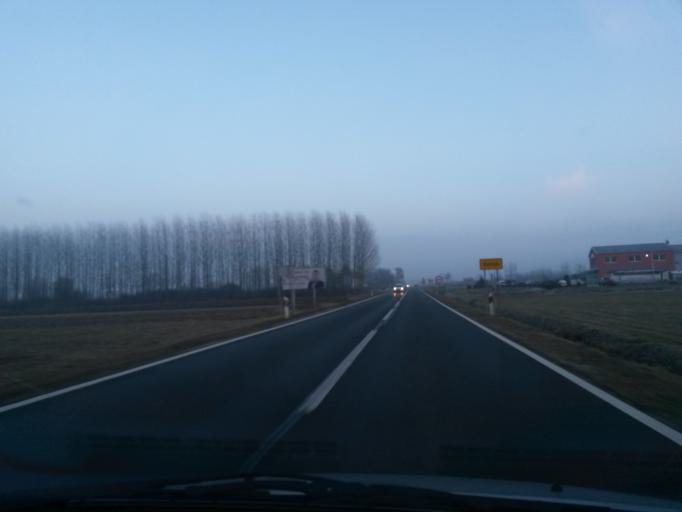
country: HR
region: Koprivnicko-Krizevacka
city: Reka
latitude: 46.2007
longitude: 16.7139
